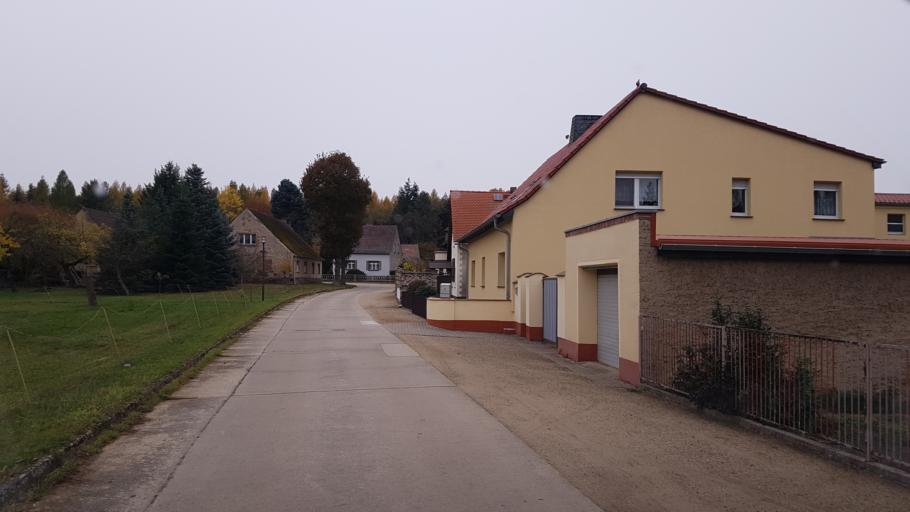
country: DE
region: Brandenburg
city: Crinitz
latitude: 51.7120
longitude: 13.7829
